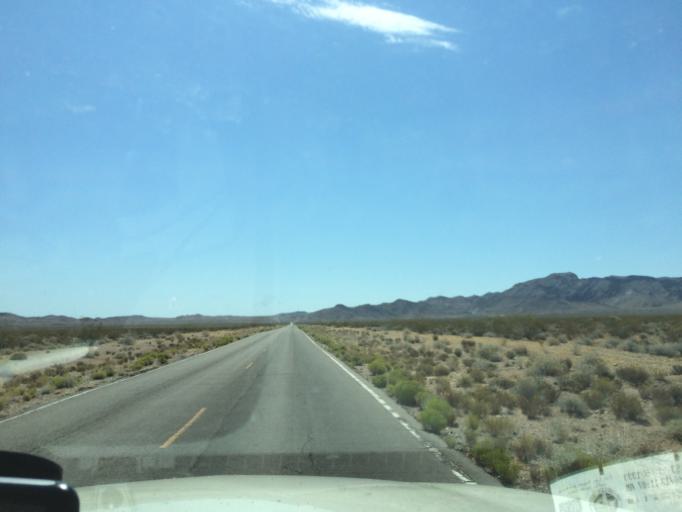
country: US
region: Nevada
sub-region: Clark County
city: Moapa Town
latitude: 36.4544
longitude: -114.7101
